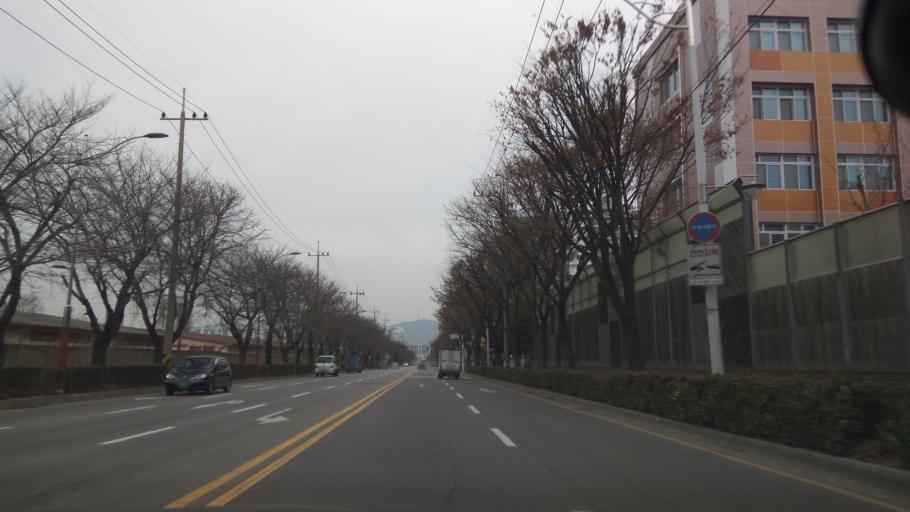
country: KR
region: Incheon
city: Incheon
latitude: 37.4918
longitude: 126.7164
